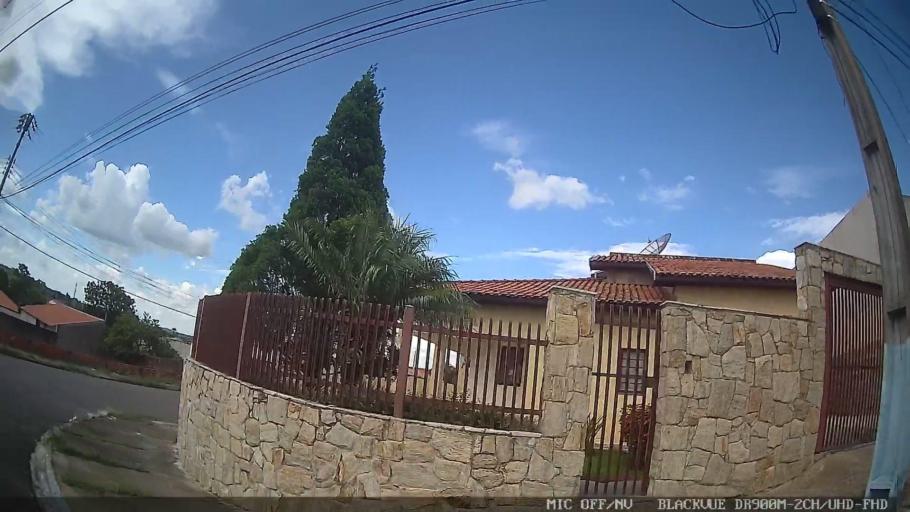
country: BR
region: Sao Paulo
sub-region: Conchas
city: Conchas
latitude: -23.0192
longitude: -48.0063
